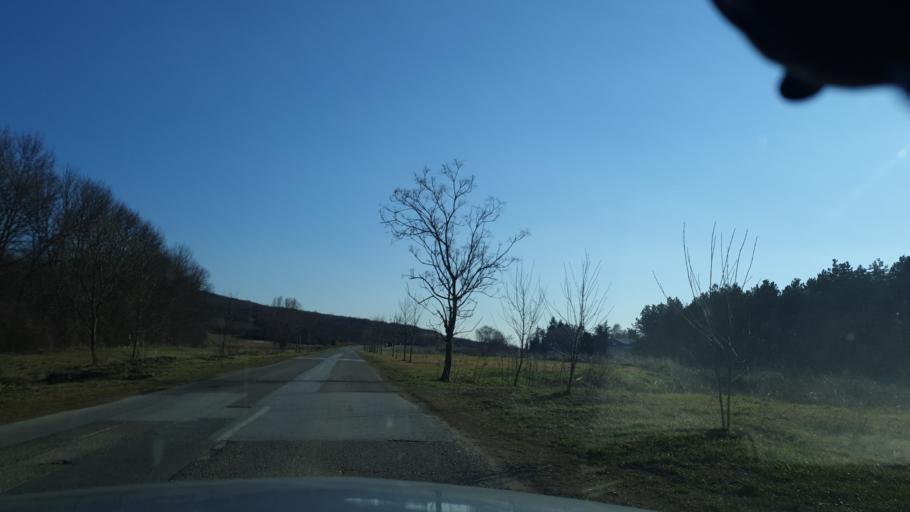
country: RS
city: Vrdnik
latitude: 45.1106
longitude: 19.8005
